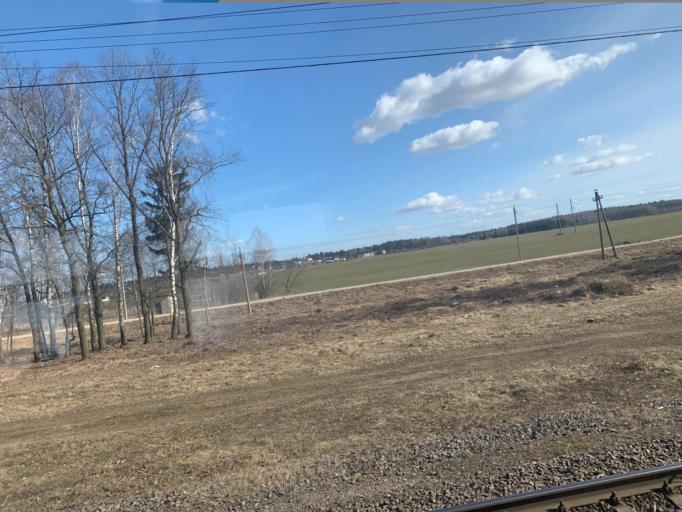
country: BY
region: Minsk
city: Shchomyslitsa
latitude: 53.8140
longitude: 27.4520
